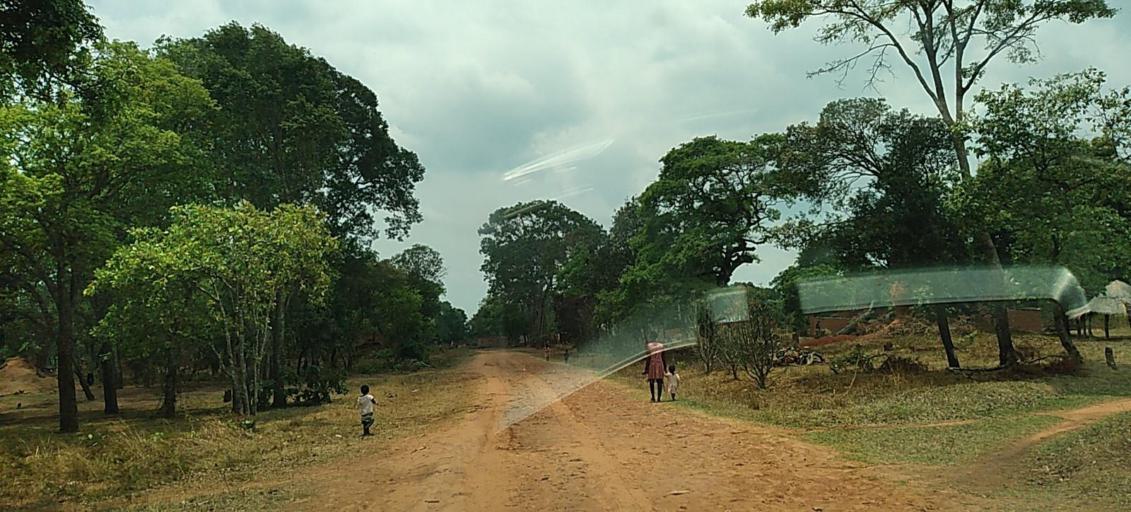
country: ZM
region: North-Western
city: Mwinilunga
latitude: -11.5195
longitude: 24.7895
